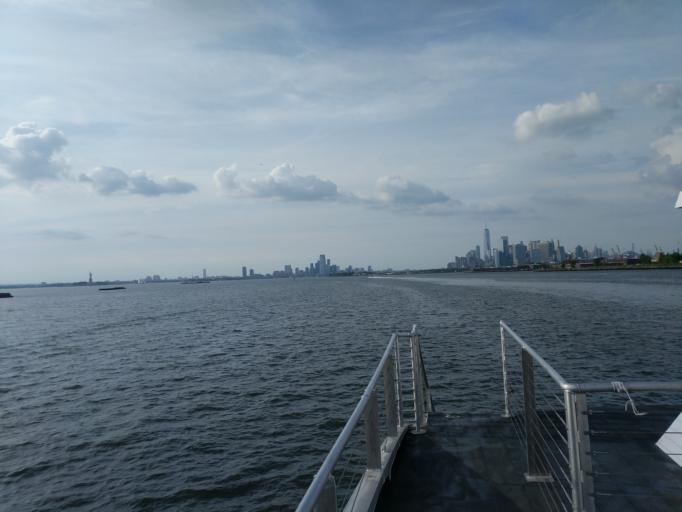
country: US
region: New York
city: New York City
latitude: 40.6640
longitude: -74.0213
